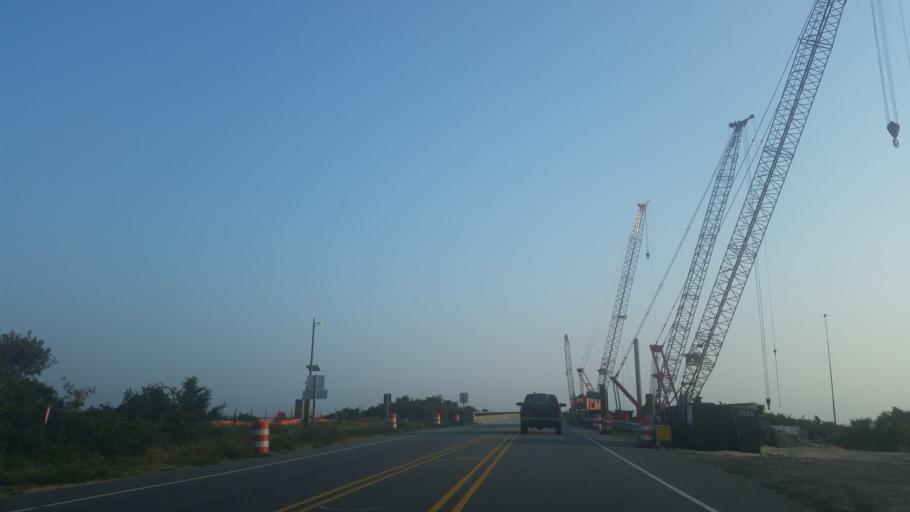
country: US
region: North Carolina
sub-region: Dare County
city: Wanchese
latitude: 35.7956
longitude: -75.5465
